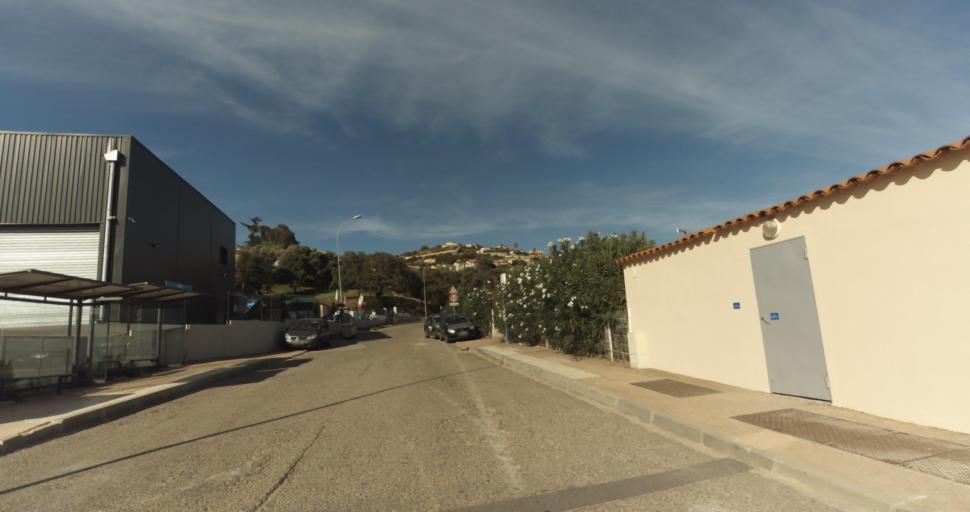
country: FR
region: Corsica
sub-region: Departement de la Corse-du-Sud
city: Afa
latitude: 41.9329
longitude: 8.7881
